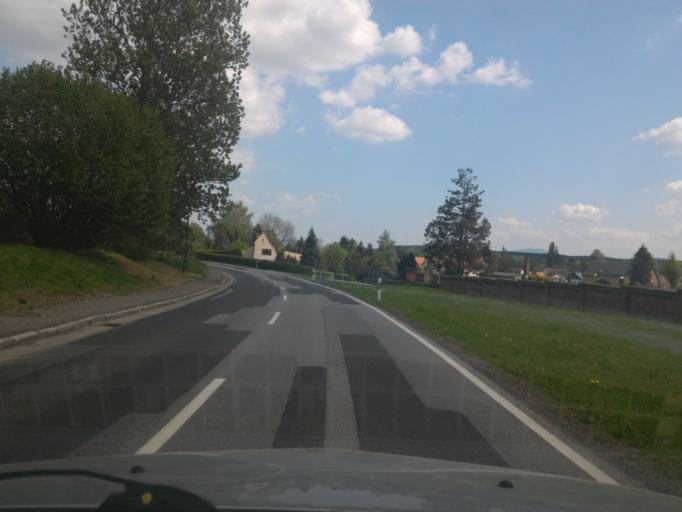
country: DE
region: Saxony
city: Bertsdorf-Hoernitz
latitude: 50.9004
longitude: 14.7449
